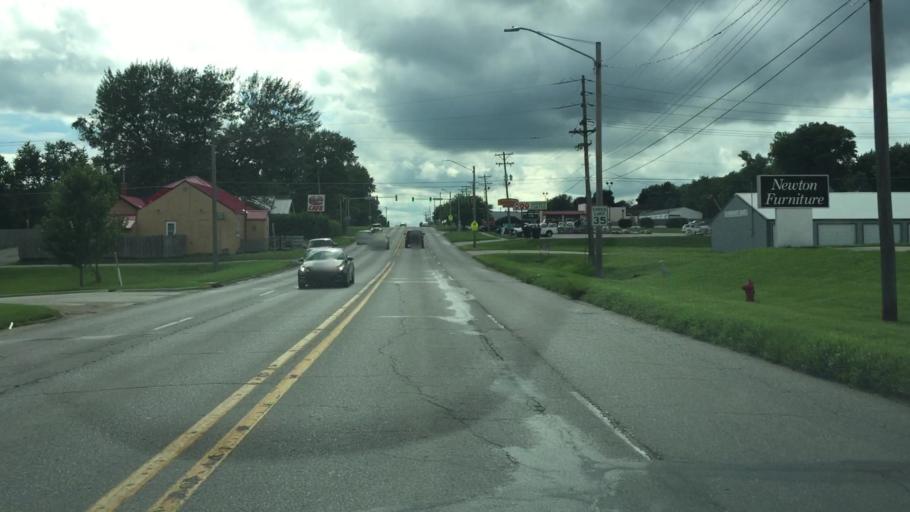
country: US
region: Iowa
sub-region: Jasper County
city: Newton
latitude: 41.6992
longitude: -93.0222
